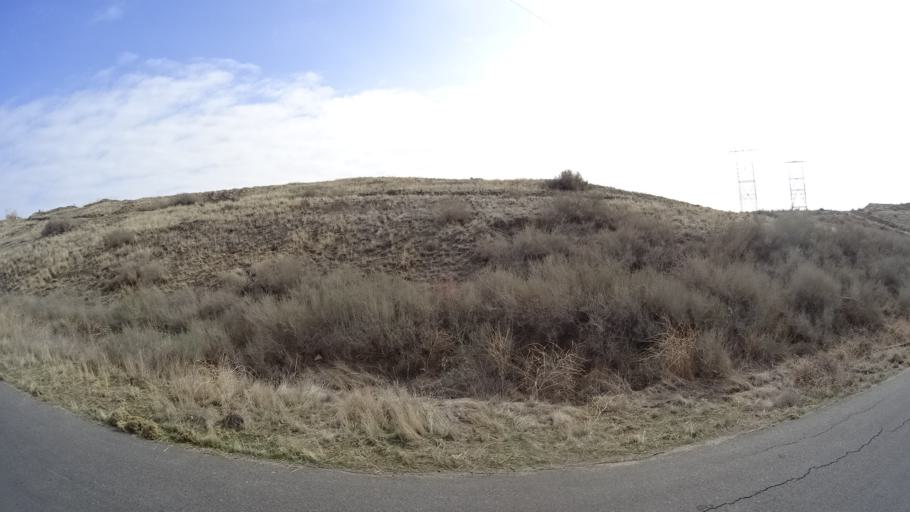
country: US
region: California
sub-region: Kern County
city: Bakersfield
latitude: 35.3929
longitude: -118.9203
